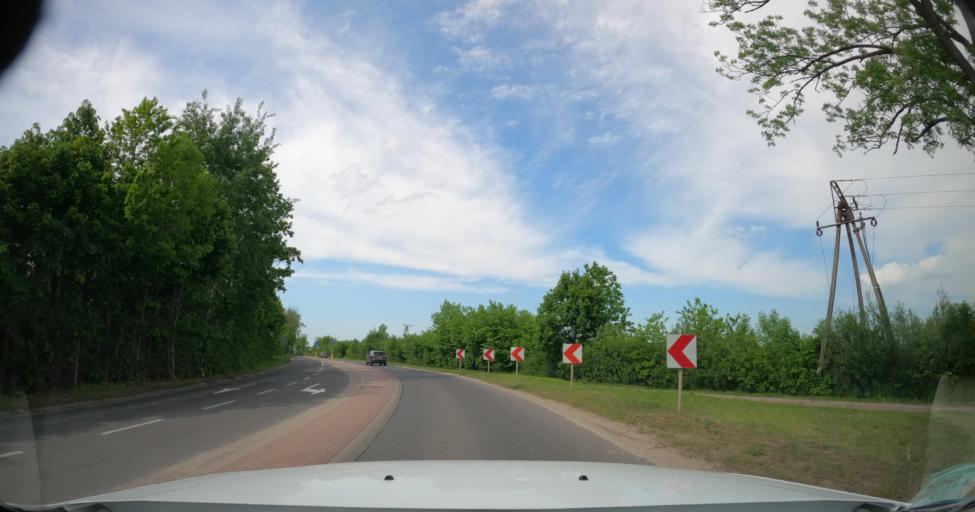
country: PL
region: Warmian-Masurian Voivodeship
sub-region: Powiat lidzbarski
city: Lidzbark Warminski
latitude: 54.1405
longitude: 20.5674
